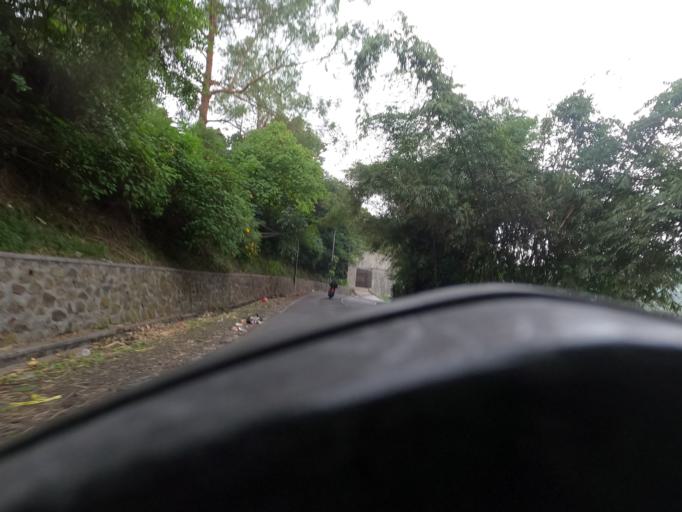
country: ID
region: West Java
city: Lembang
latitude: -6.8194
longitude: 107.6088
